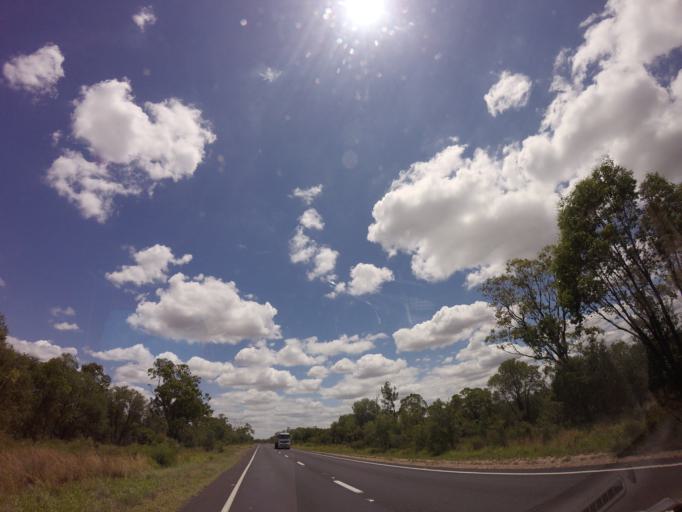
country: AU
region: New South Wales
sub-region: Moree Plains
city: Boggabilla
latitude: -28.7444
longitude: 150.2677
